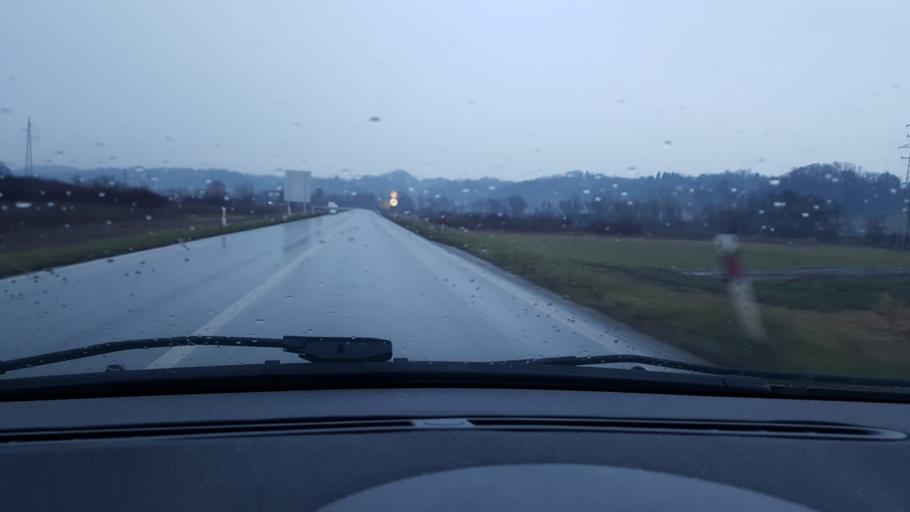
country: HR
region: Krapinsko-Zagorska
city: Zabok
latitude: 46.0297
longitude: 15.9171
